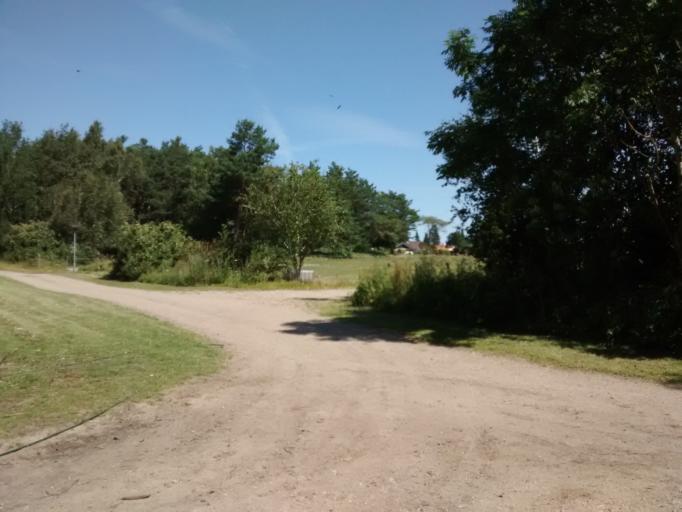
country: DK
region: Zealand
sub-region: Soro Kommune
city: Soro
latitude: 55.4494
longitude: 11.5640
